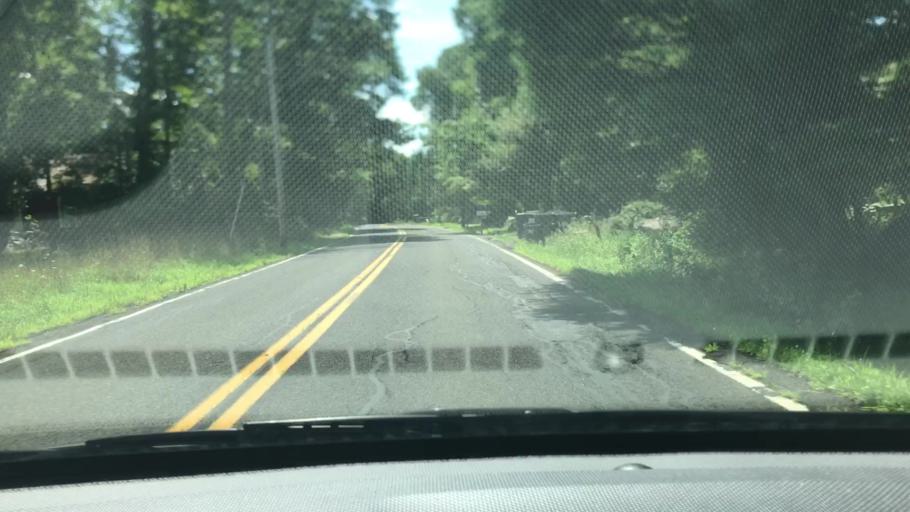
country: US
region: New York
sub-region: Ulster County
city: Stone Ridge
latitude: 41.9032
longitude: -74.1704
